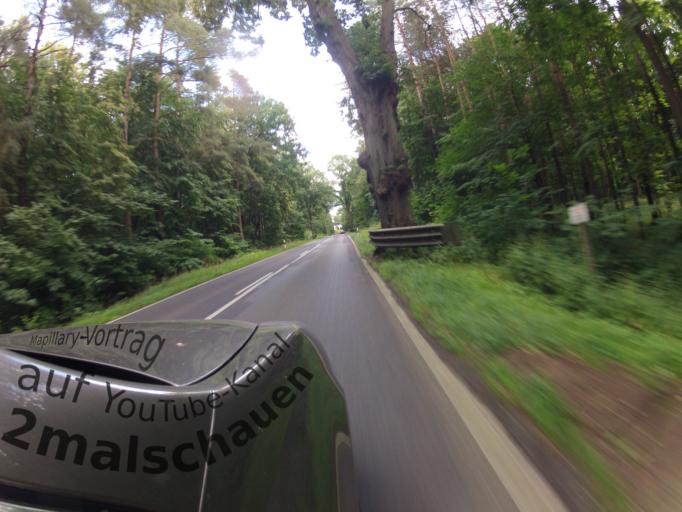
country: DE
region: Mecklenburg-Vorpommern
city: Usedom
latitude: 53.9065
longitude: 14.0308
